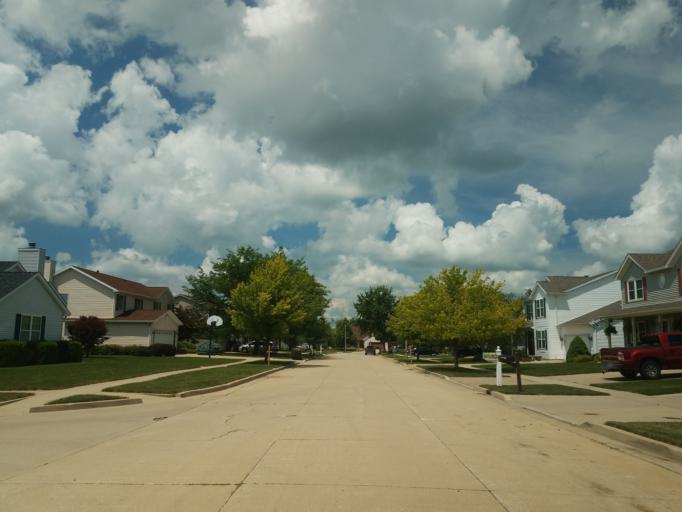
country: US
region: Illinois
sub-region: McLean County
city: Normal
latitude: 40.4991
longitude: -88.9192
